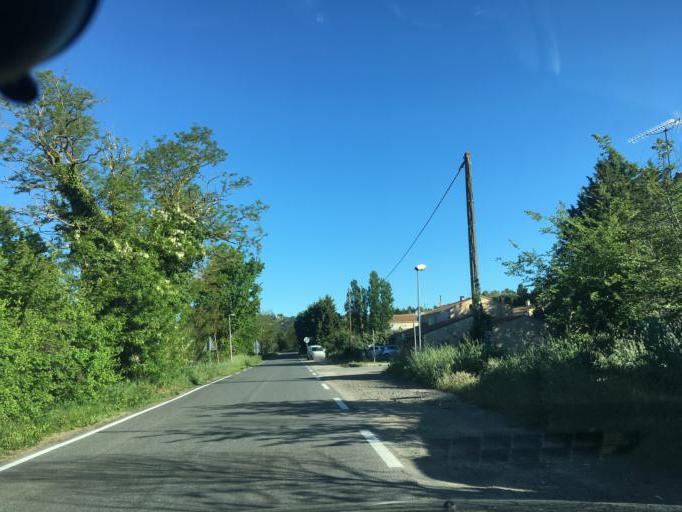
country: FR
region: Provence-Alpes-Cote d'Azur
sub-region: Departement du Var
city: Rians
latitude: 43.6078
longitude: 5.7641
